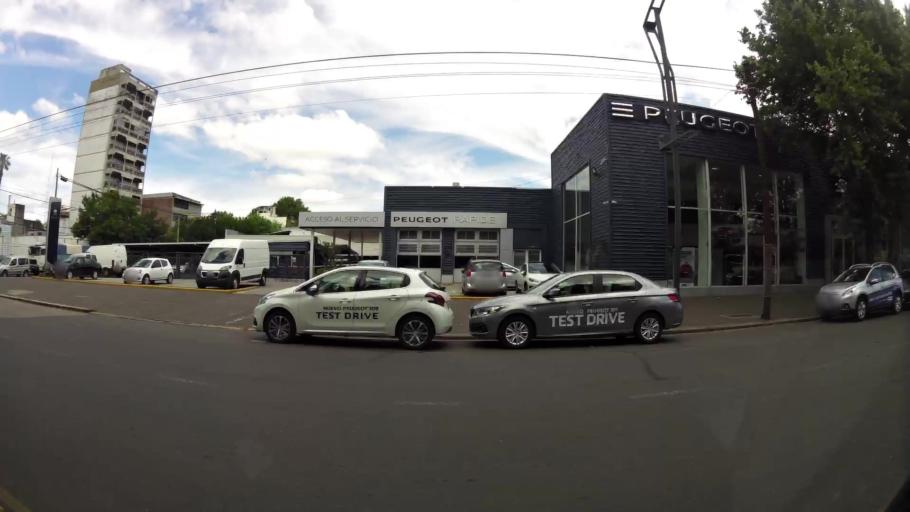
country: AR
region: Santa Fe
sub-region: Departamento de Rosario
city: Rosario
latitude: -32.9697
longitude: -60.6425
